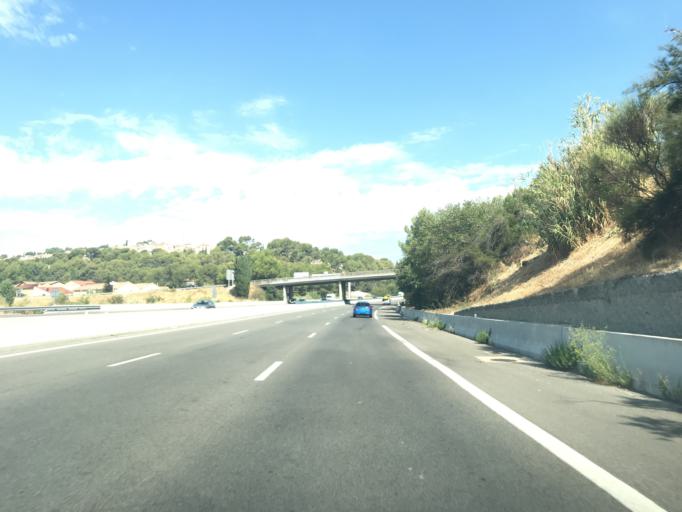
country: FR
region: Provence-Alpes-Cote d'Azur
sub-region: Departement du Var
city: Le Castellet
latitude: 43.1911
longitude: 5.7647
